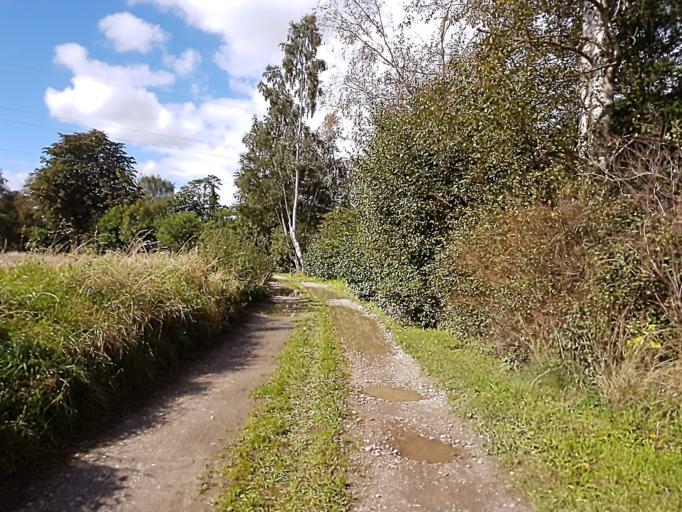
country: DK
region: Capital Region
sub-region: Egedal Kommune
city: Olstykke
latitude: 55.7897
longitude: 12.1275
